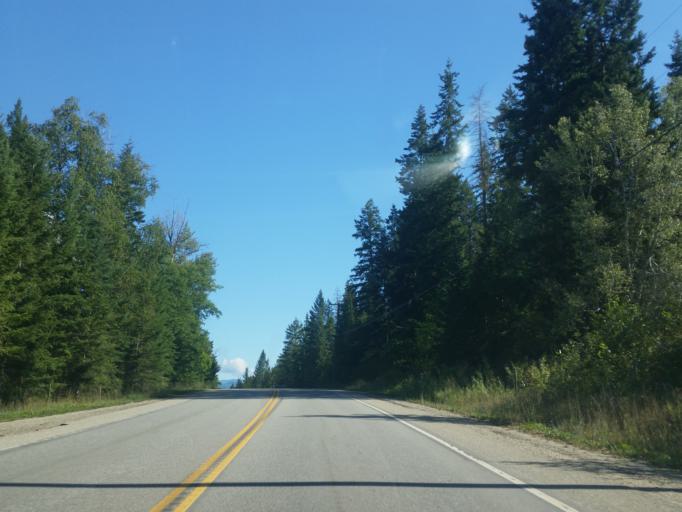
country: CA
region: British Columbia
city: Enderby
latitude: 50.6570
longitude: -119.0755
